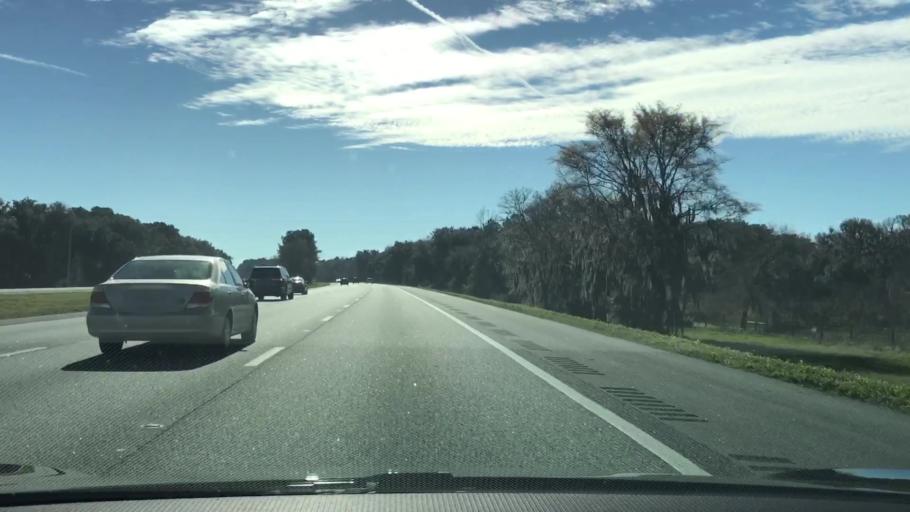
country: US
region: Florida
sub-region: Alachua County
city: Gainesville
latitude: 29.5567
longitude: -82.3446
